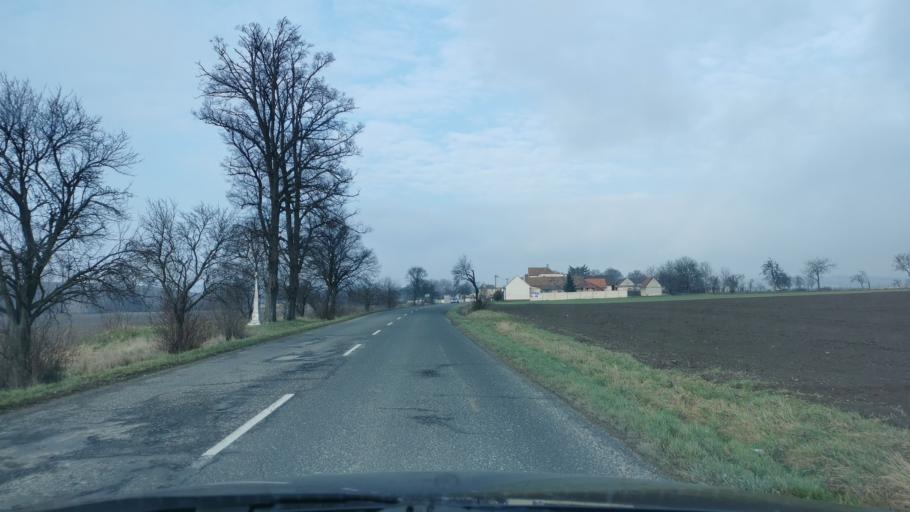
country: SK
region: Trnavsky
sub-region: Okres Senica
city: Senica
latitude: 48.7010
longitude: 17.3444
